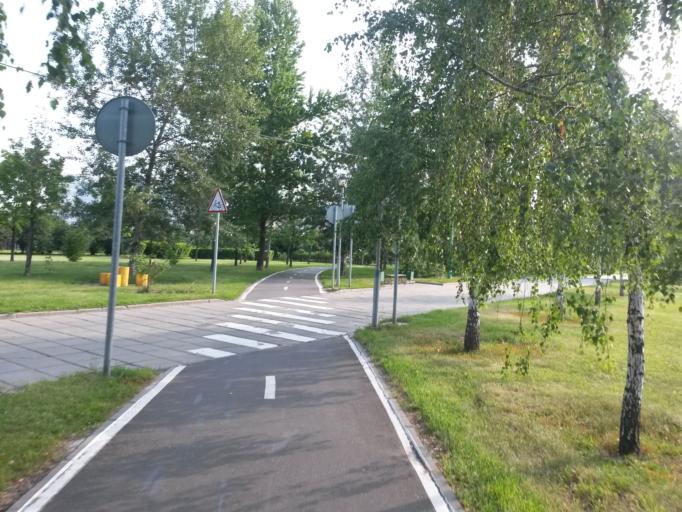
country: RU
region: Moscow
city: Brateyevo
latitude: 55.6443
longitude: 37.7569
